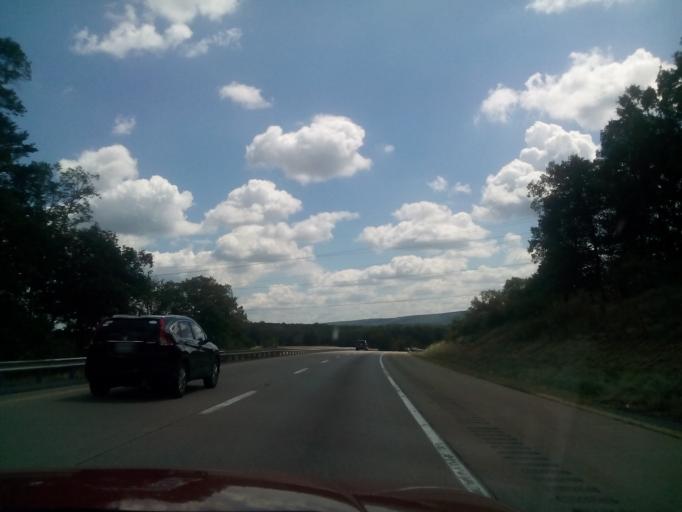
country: US
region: Pennsylvania
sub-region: Northumberland County
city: Milton
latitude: 41.0013
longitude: -76.7523
